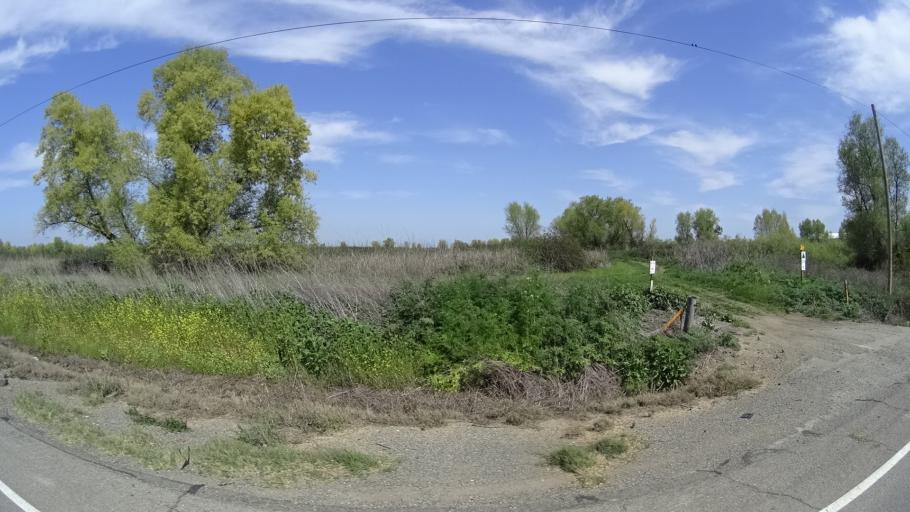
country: US
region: California
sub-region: Butte County
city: Biggs
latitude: 39.4640
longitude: -121.8877
